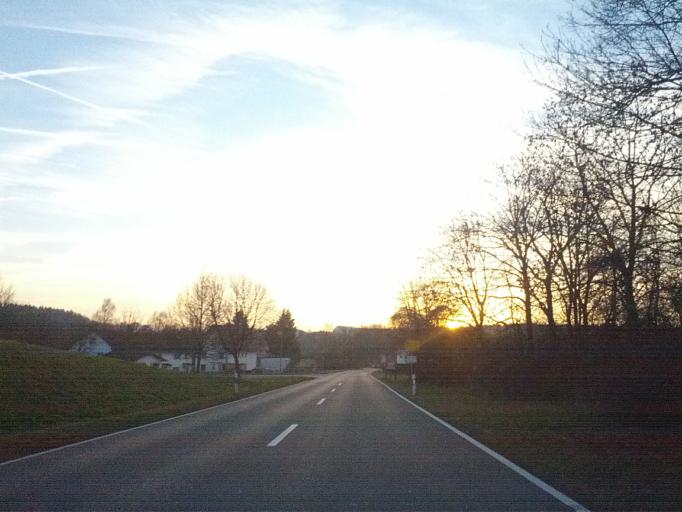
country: DE
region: Bavaria
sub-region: Swabia
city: Lautrach
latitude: 47.9059
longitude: 10.1267
